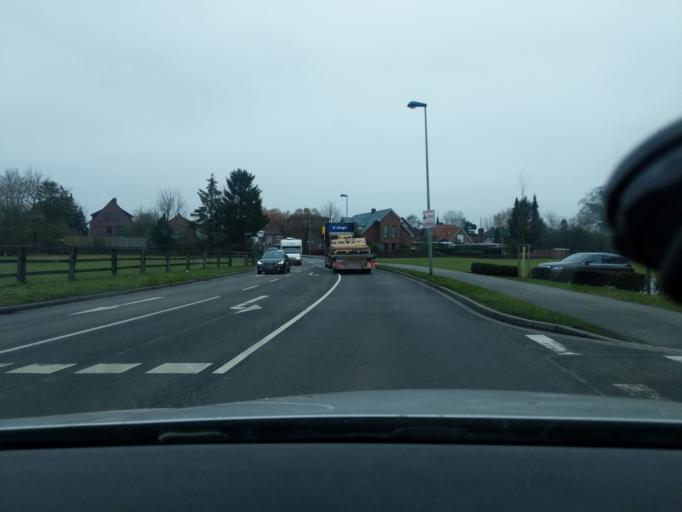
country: DE
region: Lower Saxony
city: Zeven
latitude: 53.2925
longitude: 9.2751
